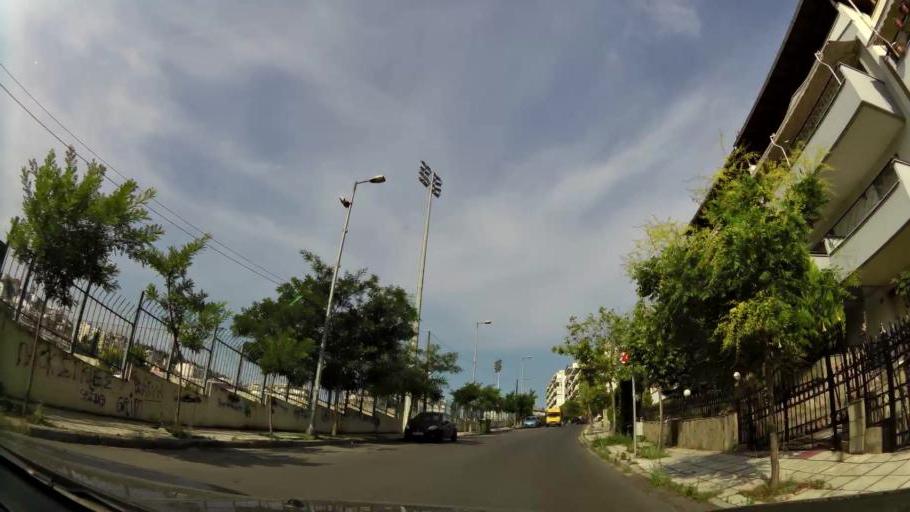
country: GR
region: Central Macedonia
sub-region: Nomos Thessalonikis
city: Sykies
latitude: 40.6525
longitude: 22.9602
